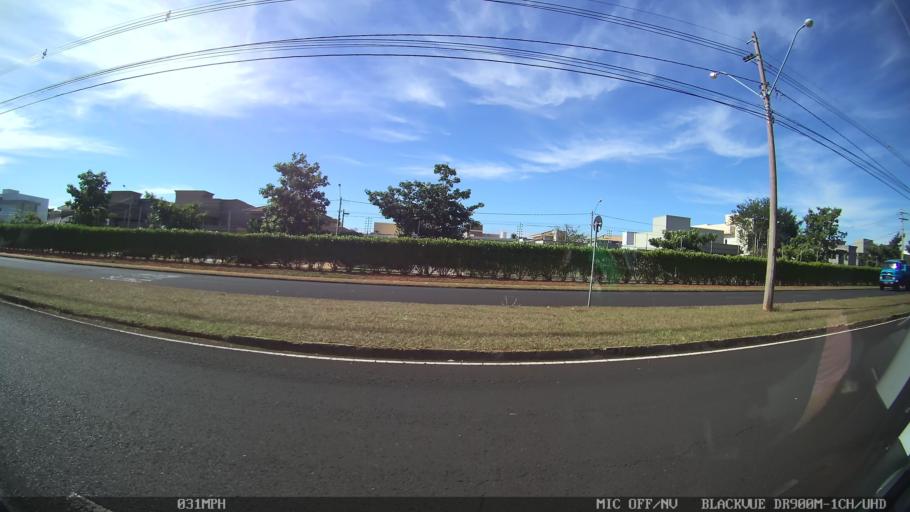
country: BR
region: Sao Paulo
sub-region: Sao Jose Do Rio Preto
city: Sao Jose do Rio Preto
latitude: -20.8079
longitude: -49.3308
